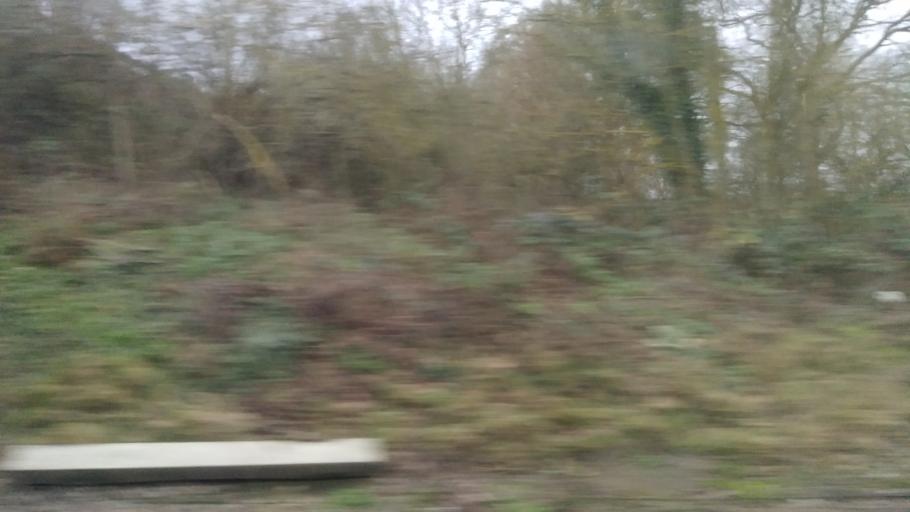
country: GB
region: England
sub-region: Kent
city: Paddock Wood
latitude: 51.1837
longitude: 0.3701
